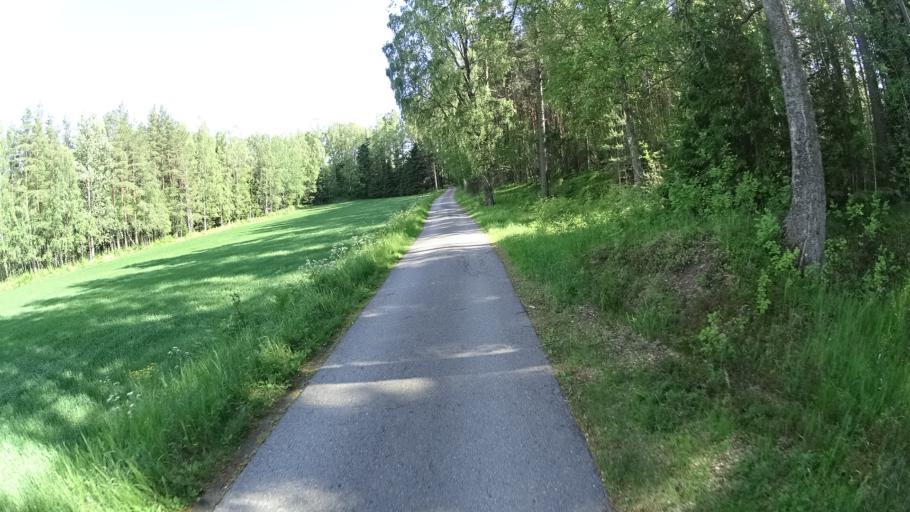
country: FI
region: Uusimaa
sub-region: Helsinki
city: Vantaa
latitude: 60.2365
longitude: 25.1824
